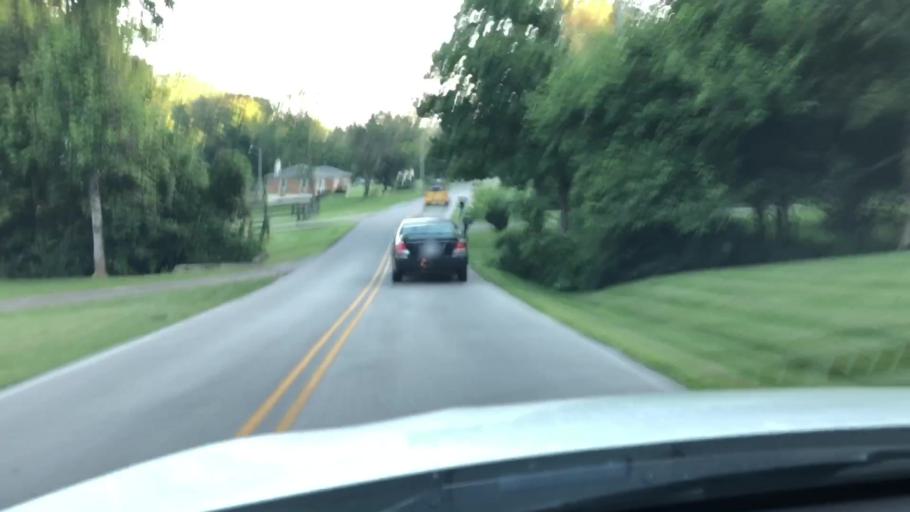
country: US
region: Kentucky
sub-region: Jefferson County
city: Middletown
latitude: 38.2000
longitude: -85.4893
